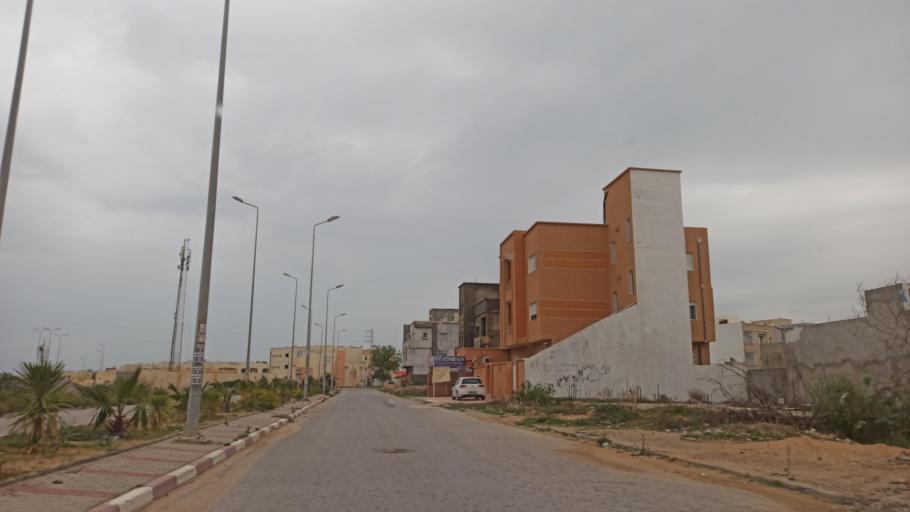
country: TN
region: Tunis
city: Hammam-Lif
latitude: 36.7097
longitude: 10.4122
